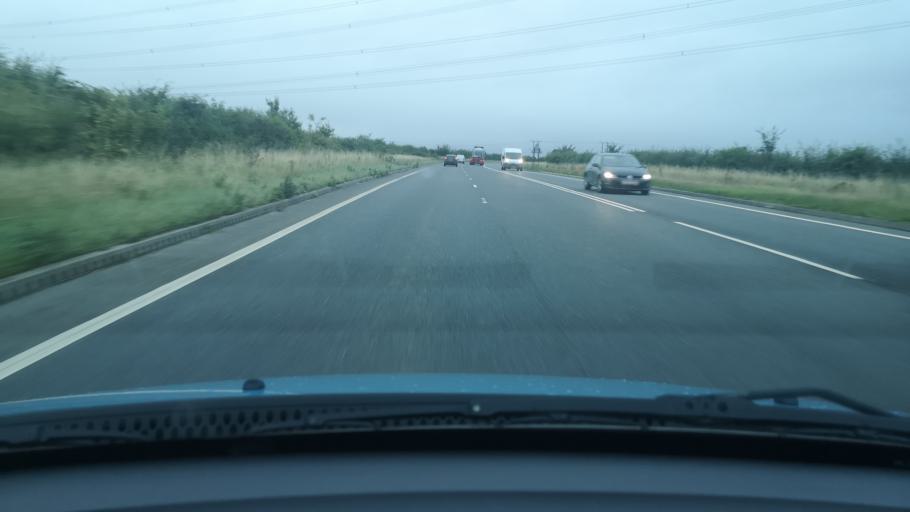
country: GB
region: England
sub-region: City and Borough of Wakefield
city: North Elmsall
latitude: 53.6149
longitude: -1.2499
